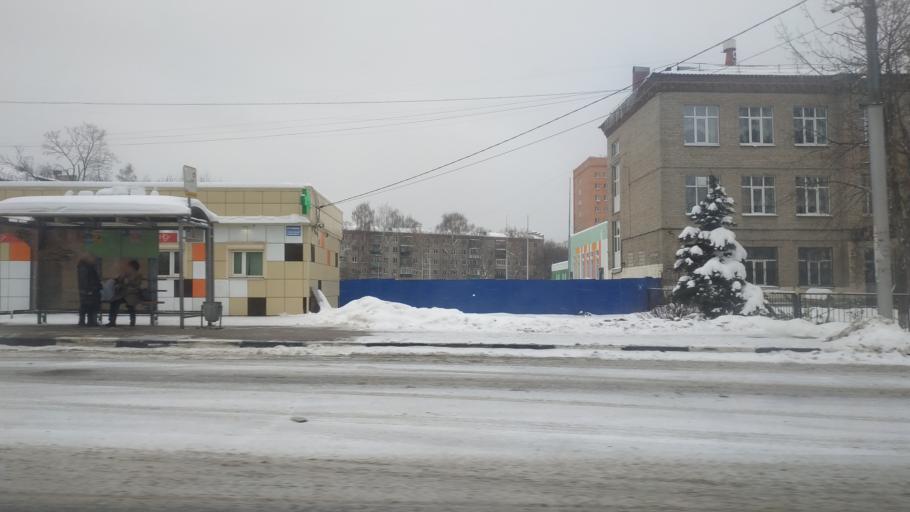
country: RU
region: Moskovskaya
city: Lyubertsy
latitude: 55.6614
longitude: 37.8662
